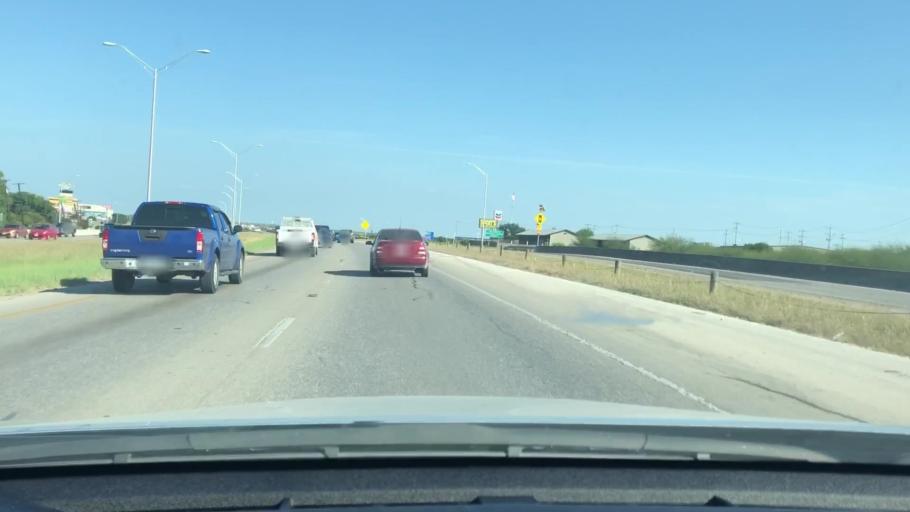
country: US
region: Texas
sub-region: Bexar County
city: Live Oak
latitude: 29.5488
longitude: -98.3199
